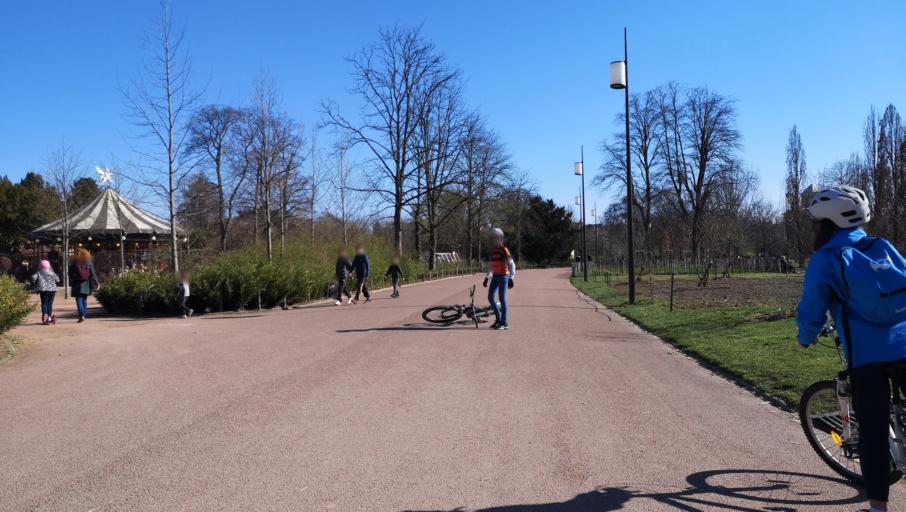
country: FR
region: Rhone-Alpes
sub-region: Departement du Rhone
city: Caluire-et-Cuire
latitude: 45.7771
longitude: 4.8529
